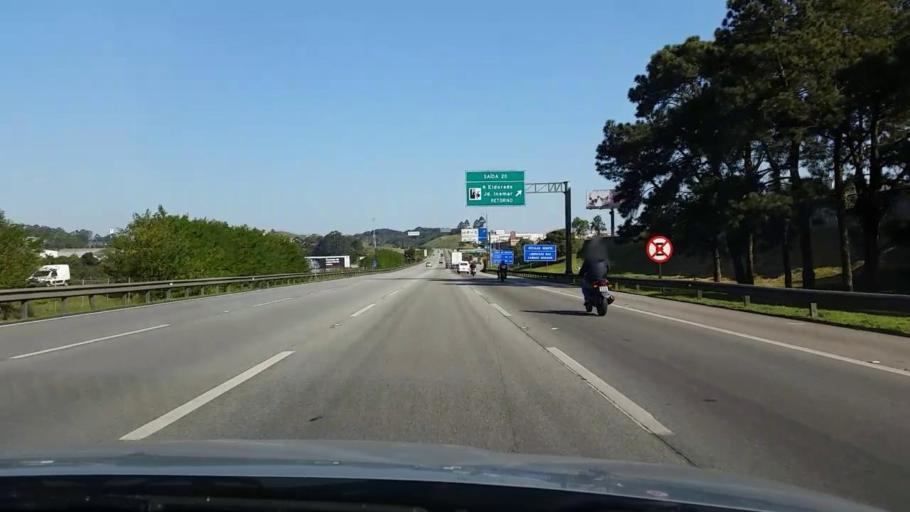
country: BR
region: Sao Paulo
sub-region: Diadema
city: Diadema
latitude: -23.7150
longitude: -46.6051
